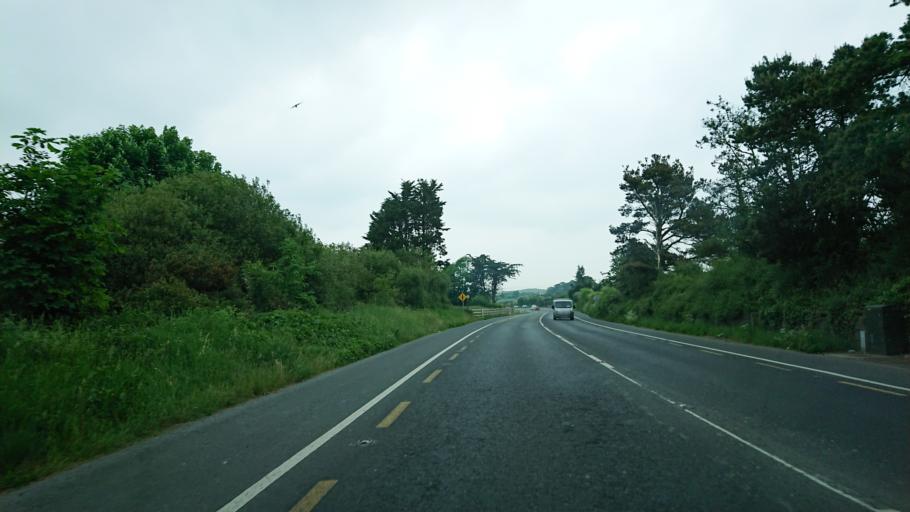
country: IE
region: Munster
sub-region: Waterford
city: Tra Mhor
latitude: 52.1945
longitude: -7.1235
